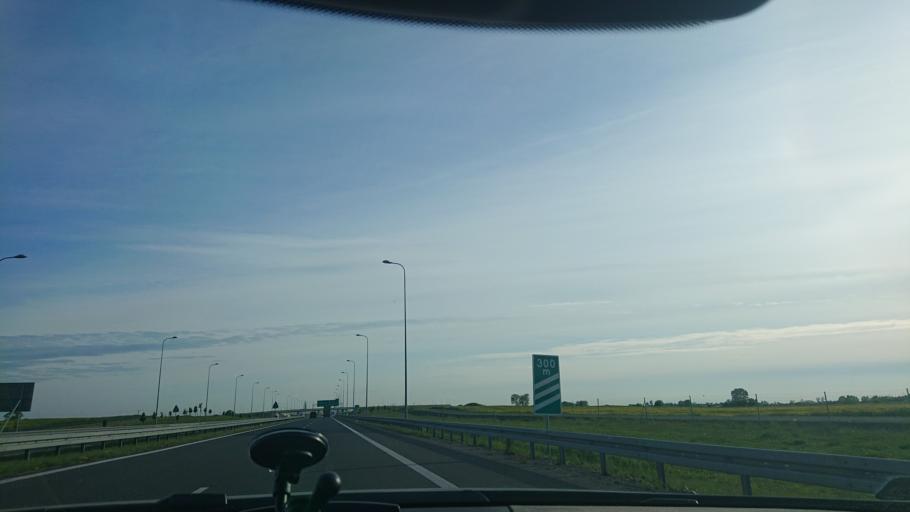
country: PL
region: Greater Poland Voivodeship
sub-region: Powiat gnieznienski
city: Lubowo
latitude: 52.5288
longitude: 17.5131
